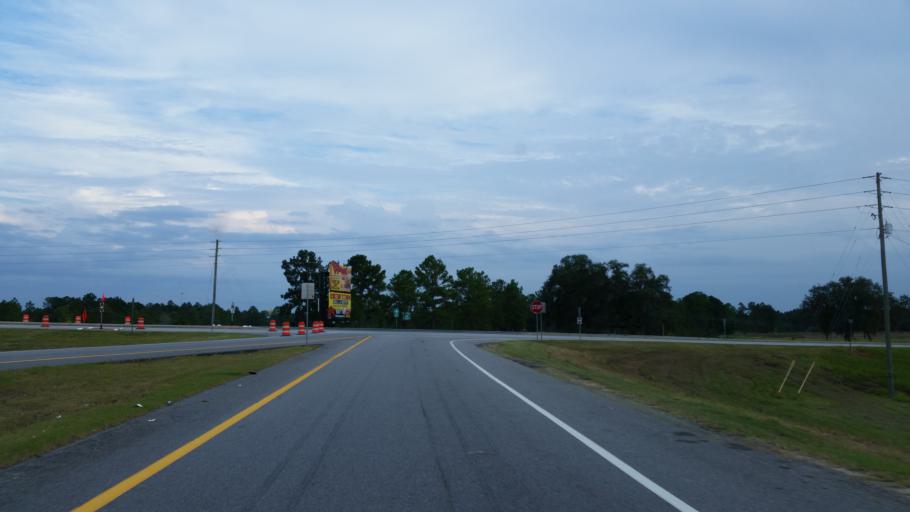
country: US
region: Georgia
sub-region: Lowndes County
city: Valdosta
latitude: 30.7767
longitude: -83.2982
